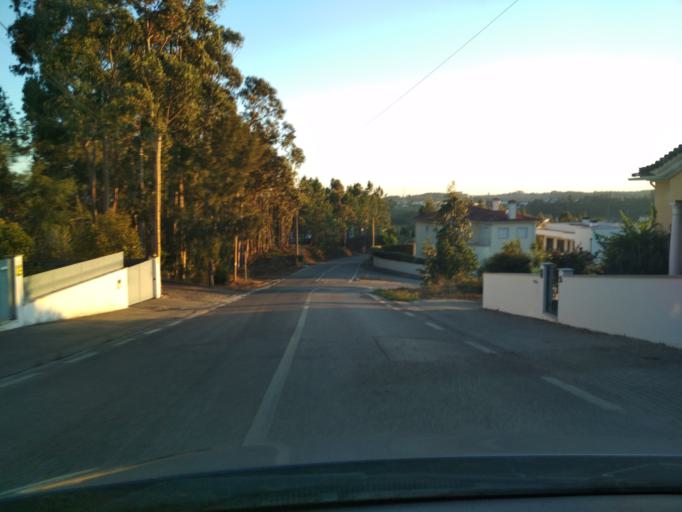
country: PT
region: Coimbra
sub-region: Condeixa-A-Nova
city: Condeixa-a-Nova
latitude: 40.1769
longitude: -8.4783
